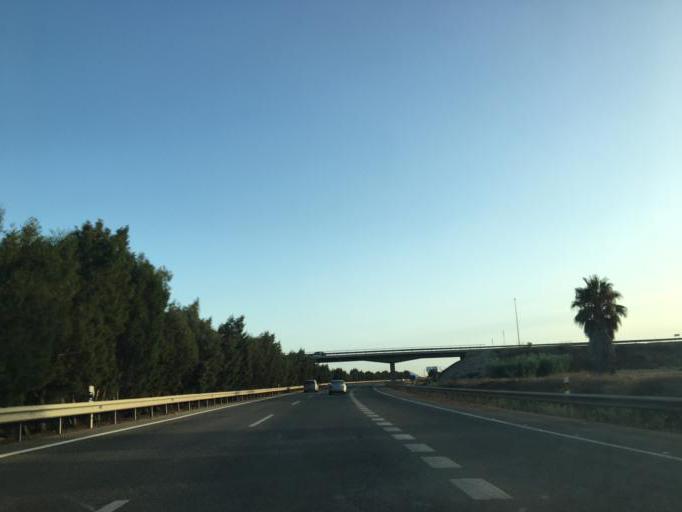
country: ES
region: Murcia
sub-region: Murcia
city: Los Alcazares
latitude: 37.6848
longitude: -0.8709
